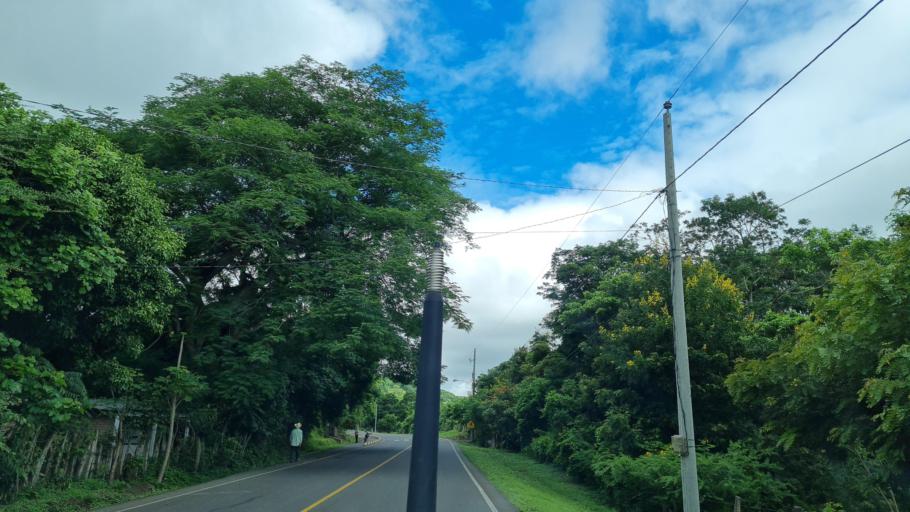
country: NI
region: Boaco
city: San Jose de los Remates
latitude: 12.5940
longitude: -85.9014
